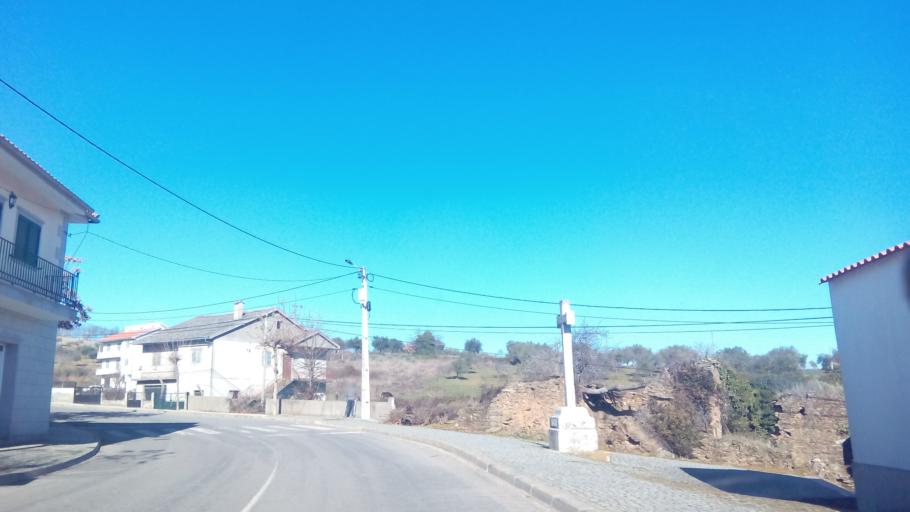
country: PT
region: Braganca
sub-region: Vimioso
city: Vimioso
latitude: 41.6452
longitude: -6.6007
